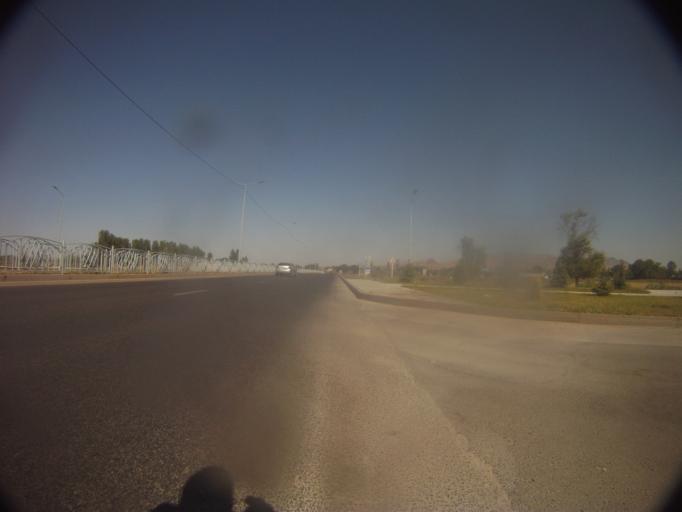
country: KZ
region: Zhambyl
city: Taraz
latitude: 42.9225
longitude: 71.4039
